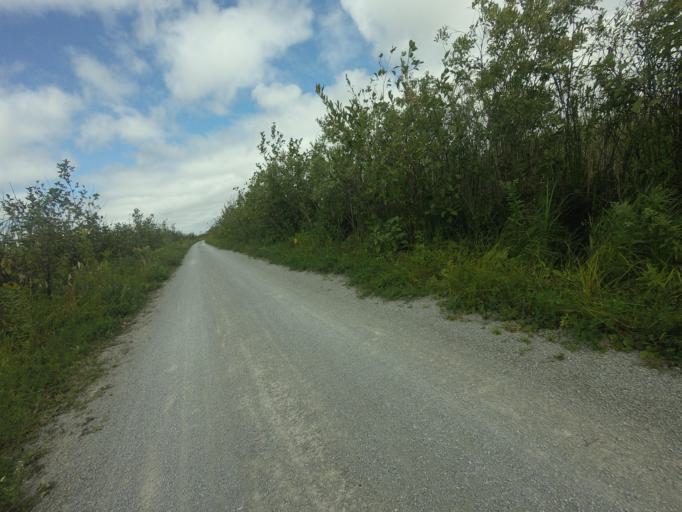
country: CA
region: Ontario
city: Uxbridge
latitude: 44.1612
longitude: -79.0807
